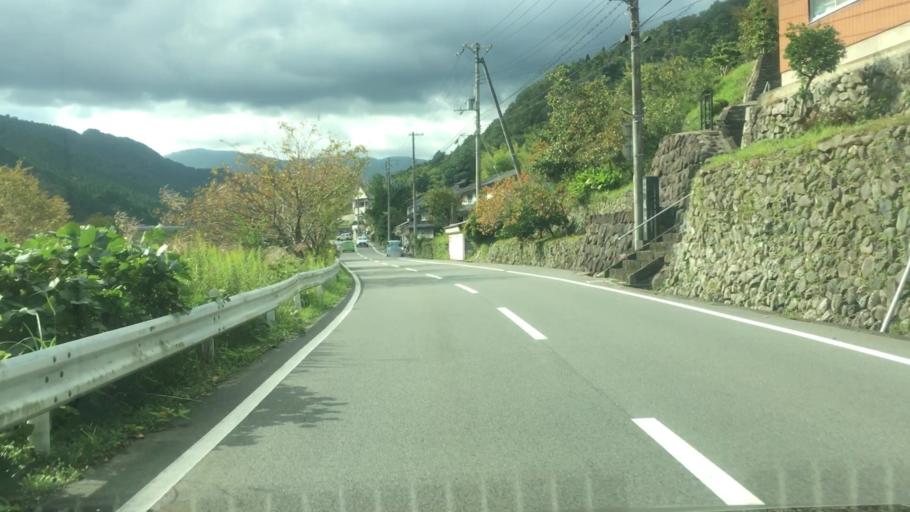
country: JP
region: Hyogo
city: Toyooka
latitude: 35.4091
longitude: 134.7537
